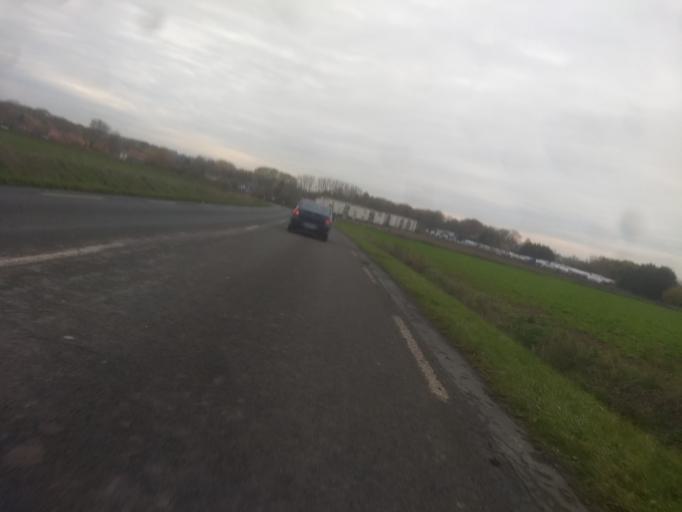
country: FR
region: Nord-Pas-de-Calais
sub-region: Departement du Pas-de-Calais
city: Achicourt
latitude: 50.2691
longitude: 2.7484
